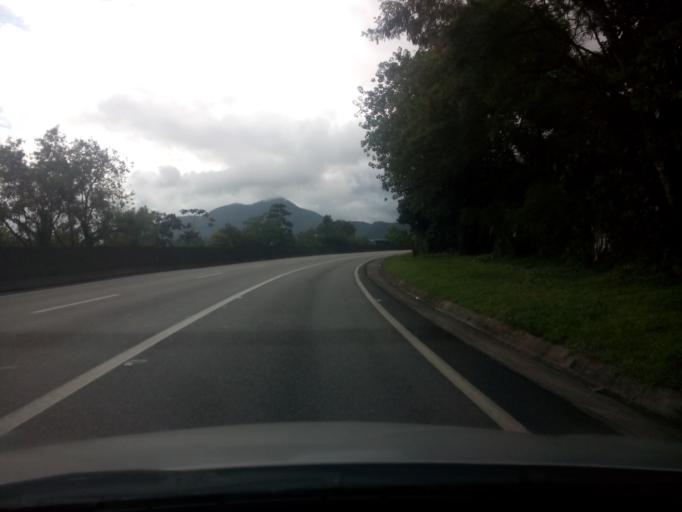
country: BR
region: Sao Paulo
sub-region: Cubatao
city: Cubatao
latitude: -23.8978
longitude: -46.4360
